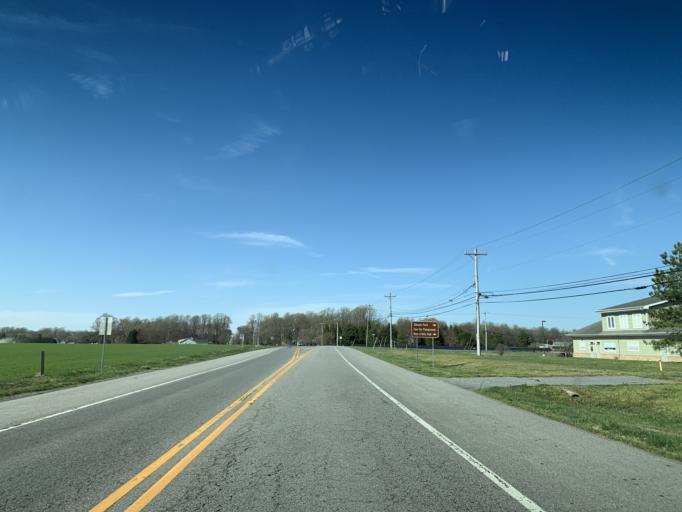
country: US
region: Delaware
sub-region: Sussex County
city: Milford
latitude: 38.9313
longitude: -75.4578
